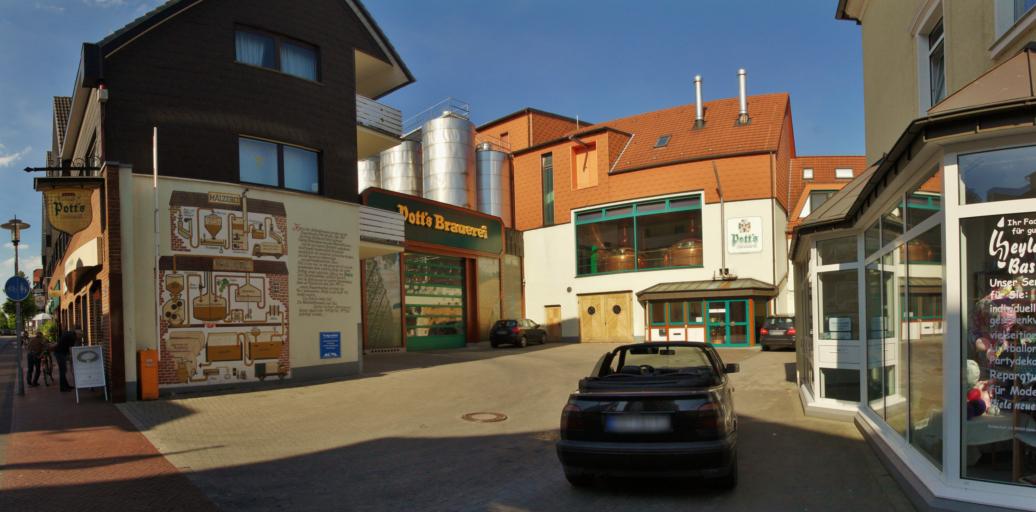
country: DE
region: North Rhine-Westphalia
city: Oelde
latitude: 51.8268
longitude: 8.1434
